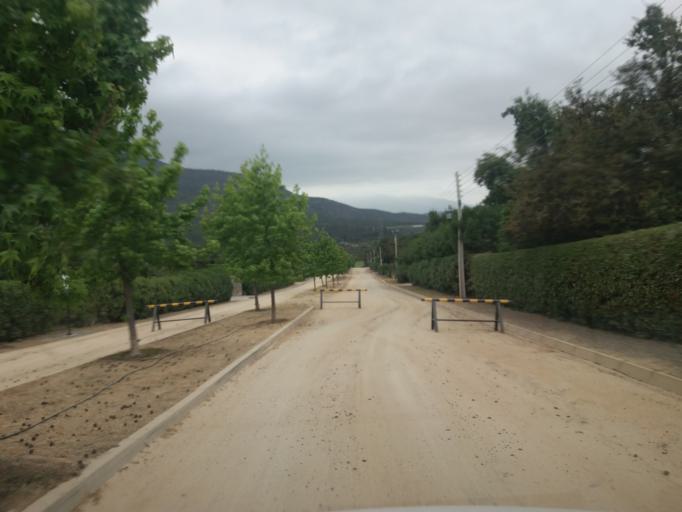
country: CL
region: Valparaiso
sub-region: Provincia de Marga Marga
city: Limache
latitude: -33.0269
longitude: -71.1337
